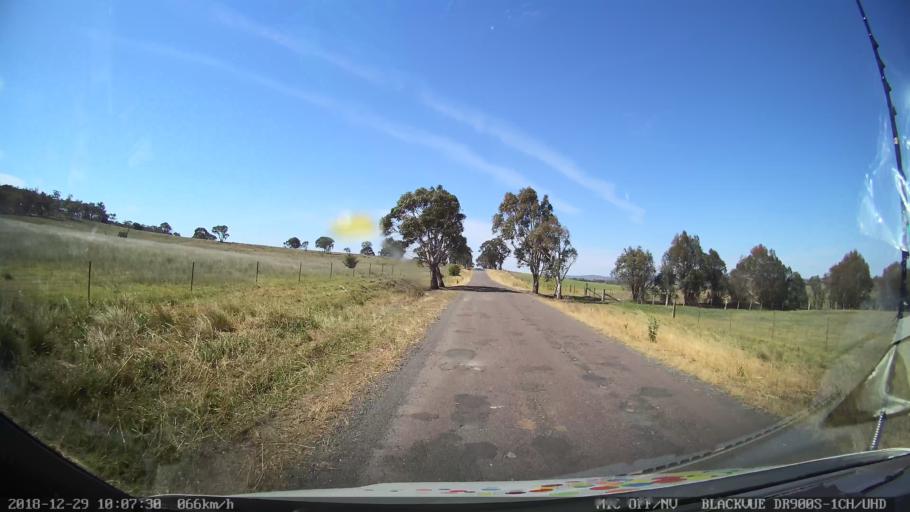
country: AU
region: New South Wales
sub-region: Yass Valley
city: Gundaroo
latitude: -34.8534
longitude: 149.4529
